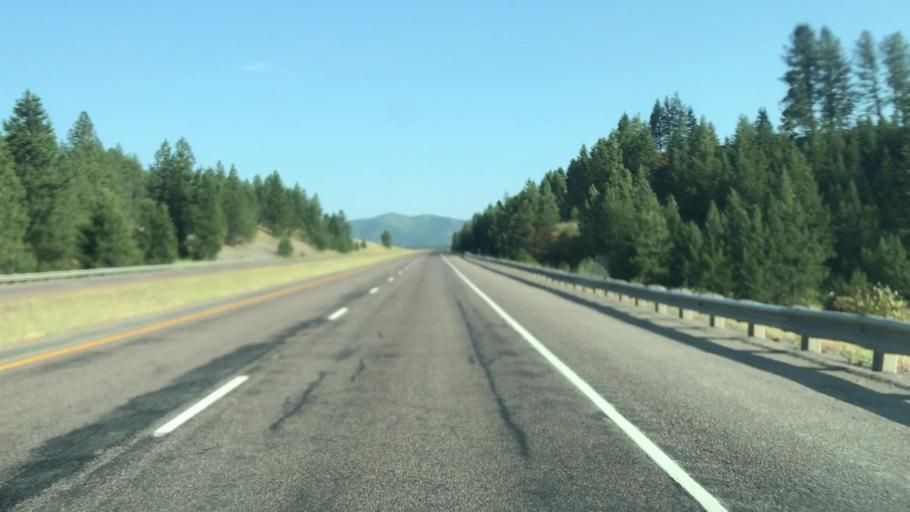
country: US
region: Montana
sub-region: Mineral County
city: Superior
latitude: 47.0531
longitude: -114.7588
